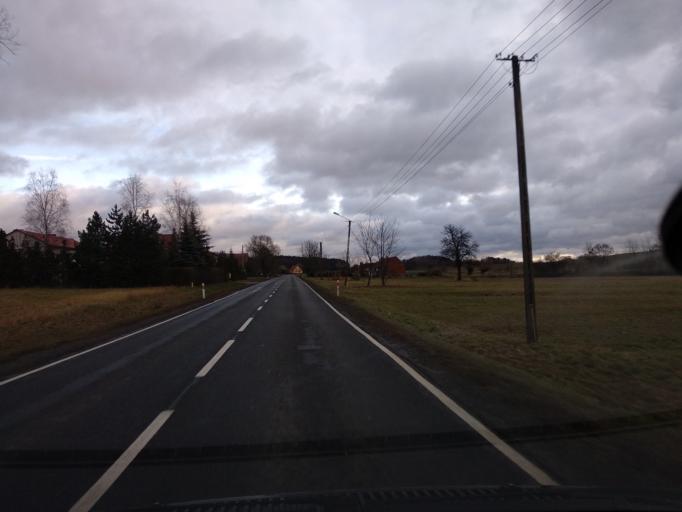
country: PL
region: Lower Silesian Voivodeship
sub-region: Powiat olesnicki
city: Miedzyborz
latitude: 51.3727
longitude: 17.6211
